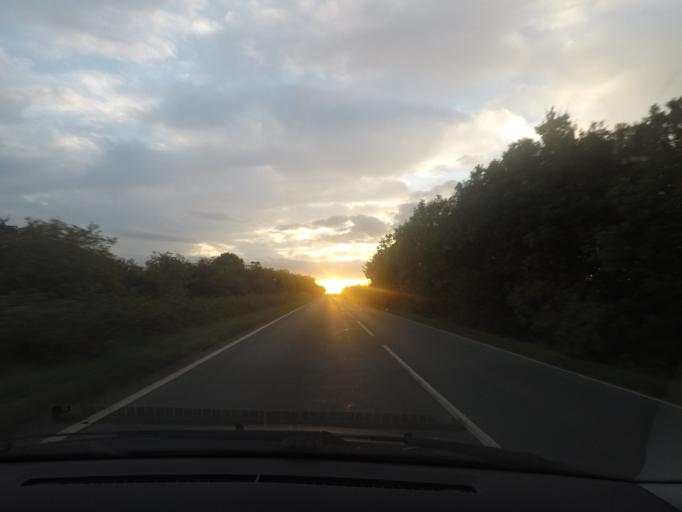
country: GB
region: England
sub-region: North Lincolnshire
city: Croxton
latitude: 53.5828
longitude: -0.3282
